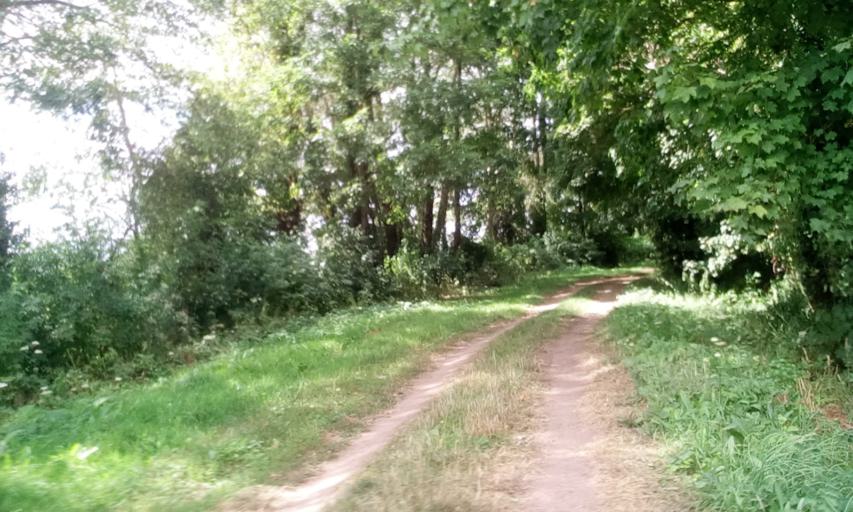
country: FR
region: Lower Normandy
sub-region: Departement du Calvados
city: Sannerville
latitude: 49.1594
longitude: -0.2125
